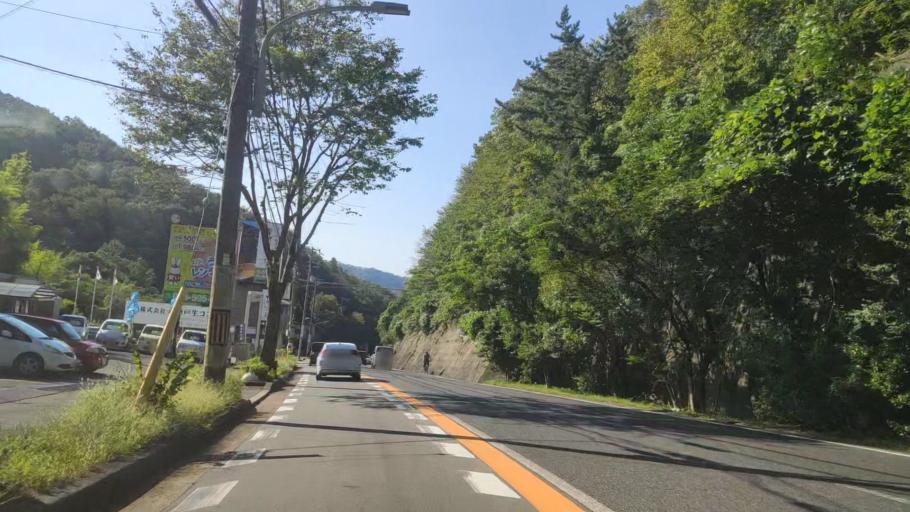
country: JP
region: Hyogo
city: Kobe
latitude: 34.7354
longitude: 135.1586
